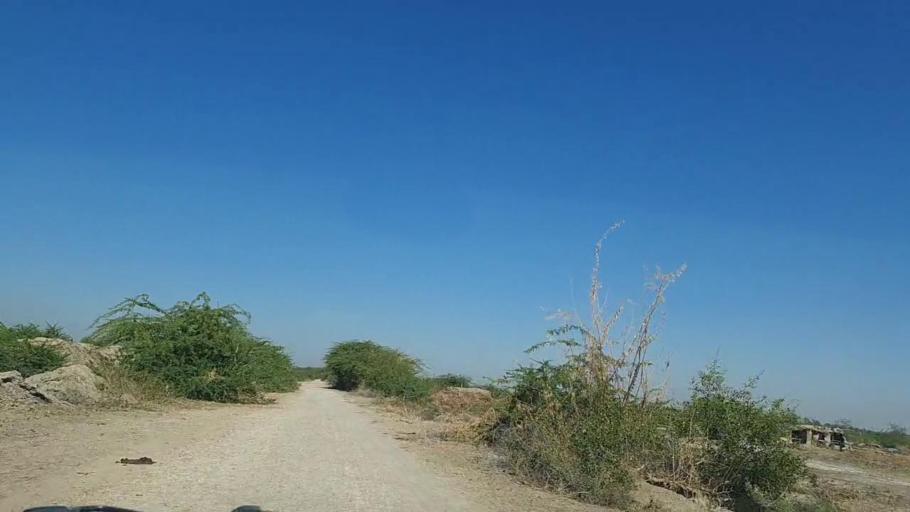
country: PK
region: Sindh
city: Dhoro Naro
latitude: 25.4650
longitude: 69.5131
